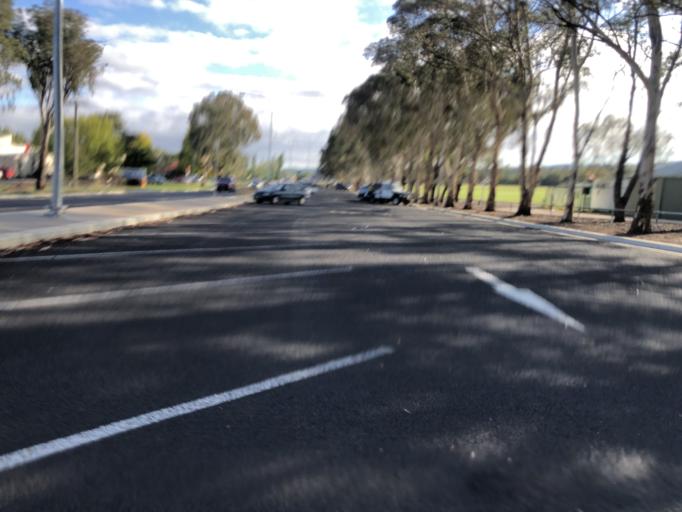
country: AU
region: New South Wales
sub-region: Orange Municipality
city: Orange
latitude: -33.3089
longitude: 149.0971
